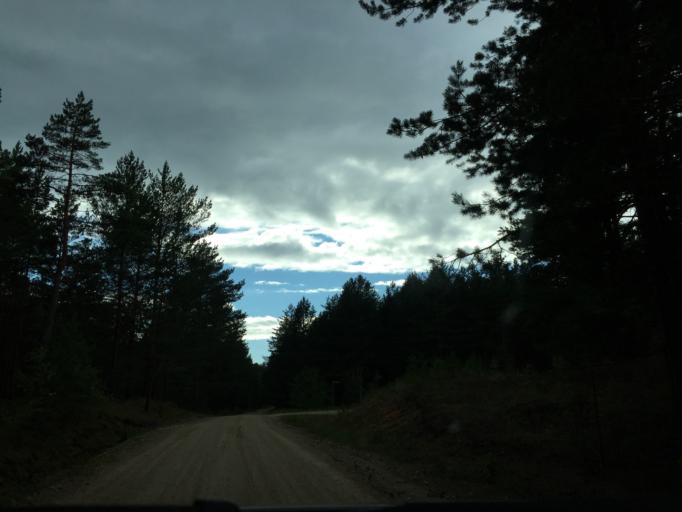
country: LV
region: Saulkrastu
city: Saulkrasti
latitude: 57.1732
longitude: 24.3792
